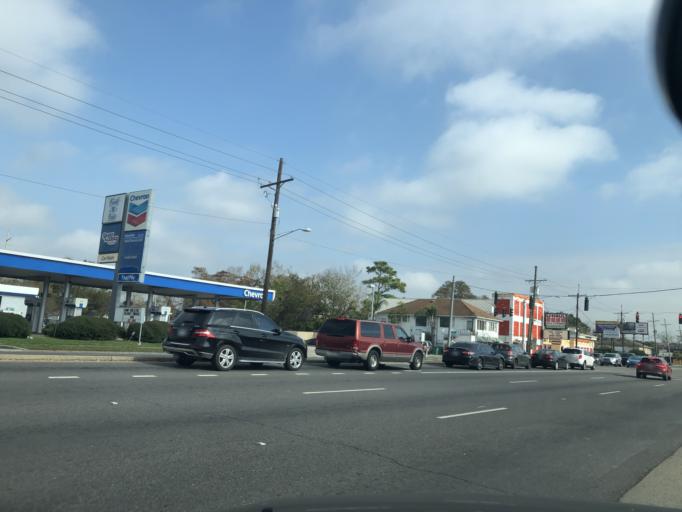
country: US
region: Louisiana
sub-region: Jefferson Parish
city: Metairie Terrace
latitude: 29.9751
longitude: -90.1702
